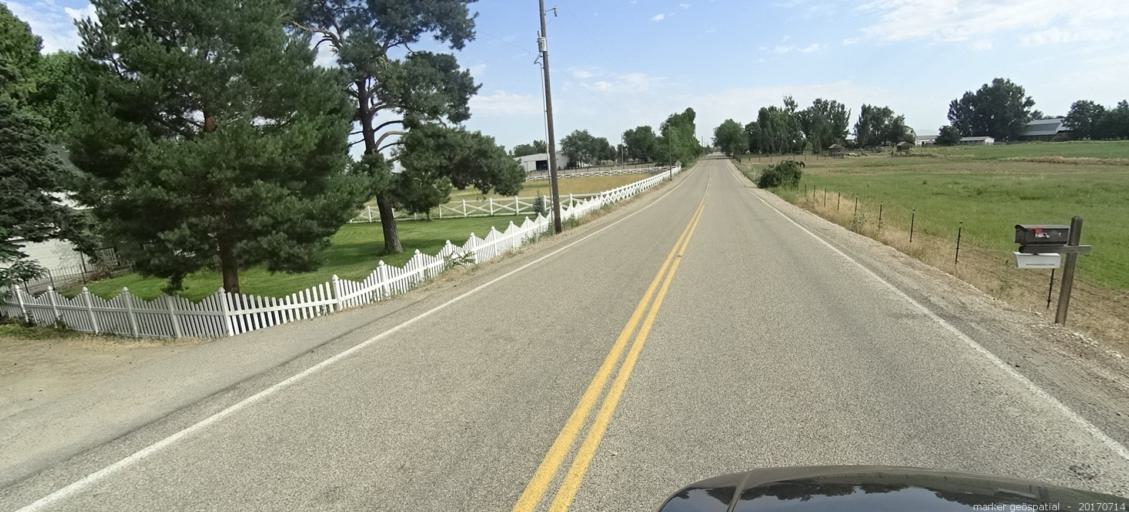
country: US
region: Idaho
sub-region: Ada County
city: Kuna
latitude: 43.4891
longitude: -116.3544
